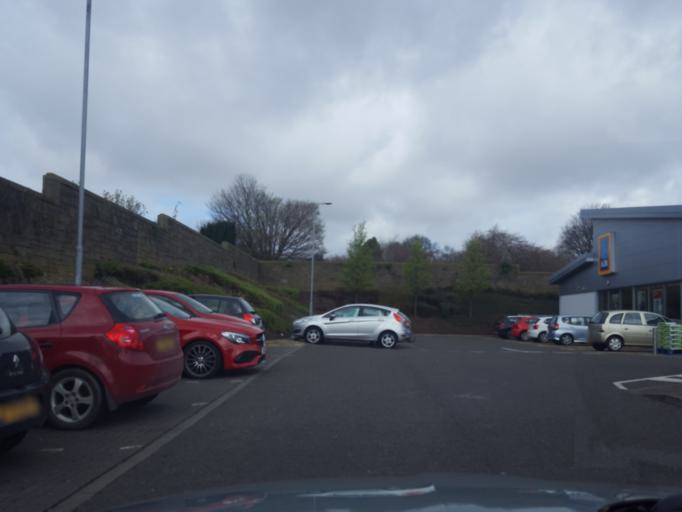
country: GB
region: Scotland
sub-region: Fife
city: Newport-On-Tay
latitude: 56.4733
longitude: -2.9303
